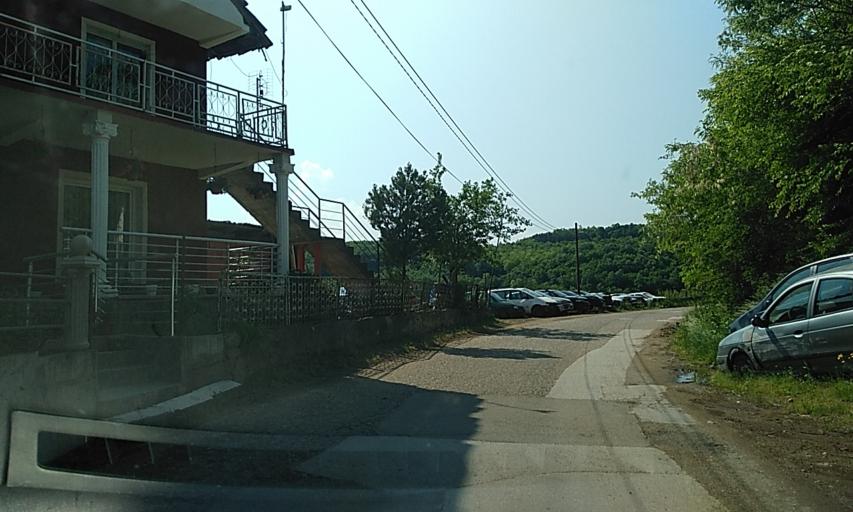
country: RS
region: Central Serbia
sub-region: Pcinjski Okrug
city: Vladicin Han
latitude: 42.7208
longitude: 22.0668
